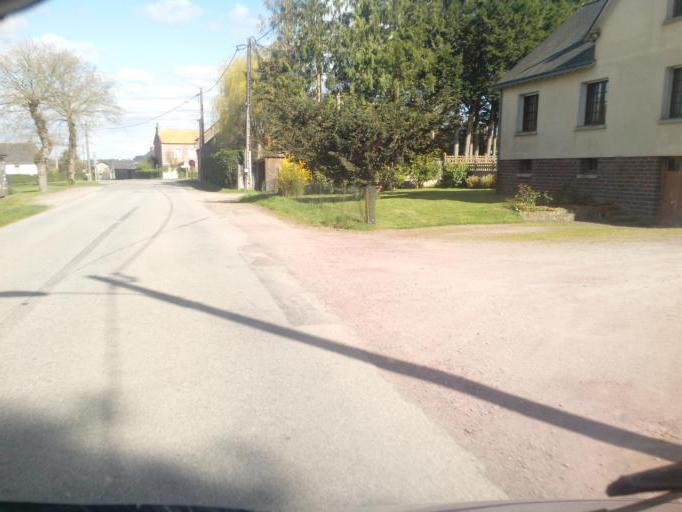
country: FR
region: Brittany
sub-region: Departement d'Ille-et-Vilaine
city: Paimpont
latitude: 48.0661
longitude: -2.1907
